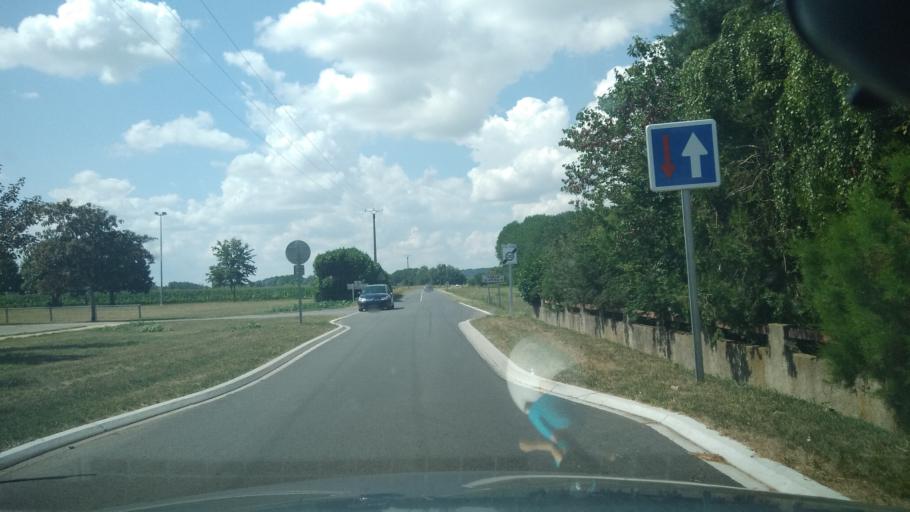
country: FR
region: Poitou-Charentes
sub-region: Departement de la Vienne
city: Dange-Saint-Romain
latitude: 46.9302
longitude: 0.5933
